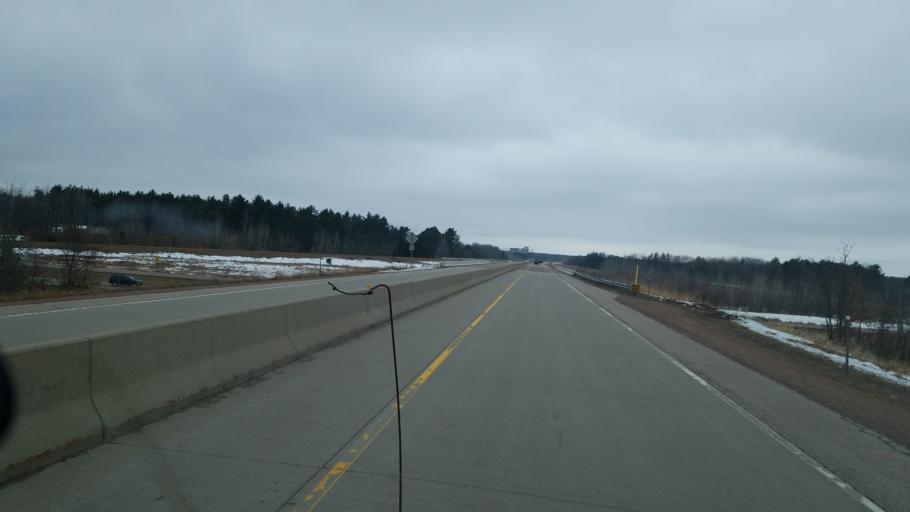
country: US
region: Wisconsin
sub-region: Portage County
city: Stevens Point
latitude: 44.5980
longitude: -89.6134
